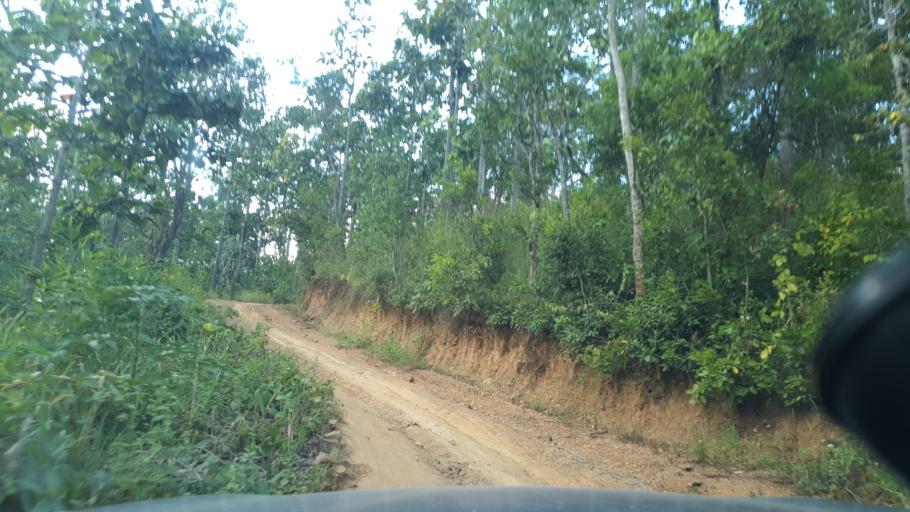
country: TH
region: Chiang Mai
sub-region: Amphoe Chiang Dao
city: Chiang Dao
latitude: 19.4100
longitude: 98.8322
